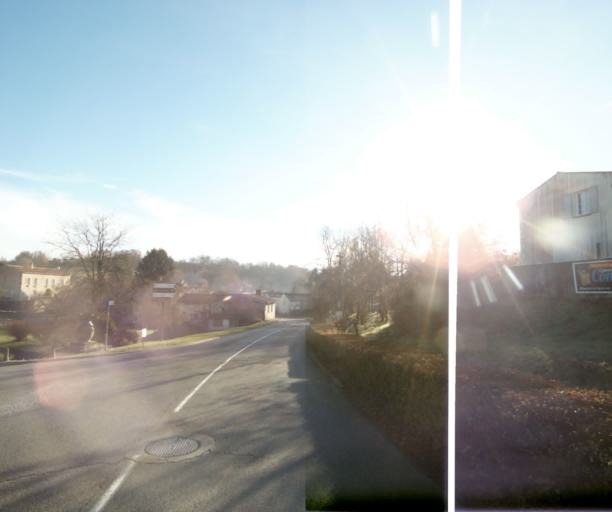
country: FR
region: Poitou-Charentes
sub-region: Departement de la Charente-Maritime
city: Chaniers
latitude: 45.7595
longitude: -0.5428
